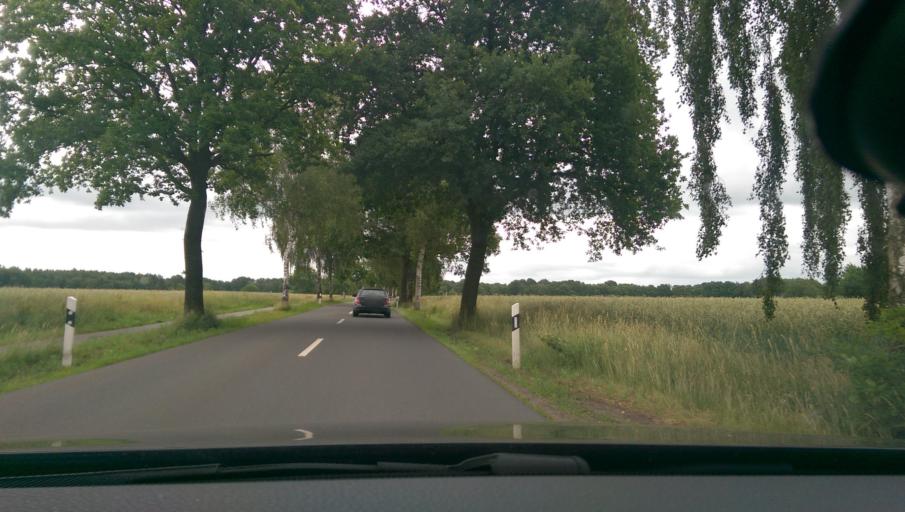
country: DE
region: Lower Saxony
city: Horstedt
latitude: 53.1757
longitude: 9.2703
